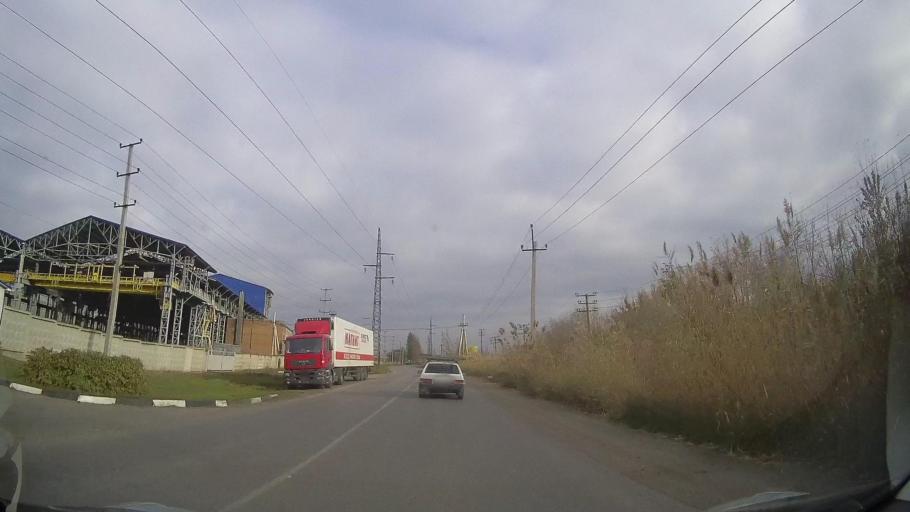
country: RU
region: Rostov
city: Bataysk
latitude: 47.1131
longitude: 39.7665
